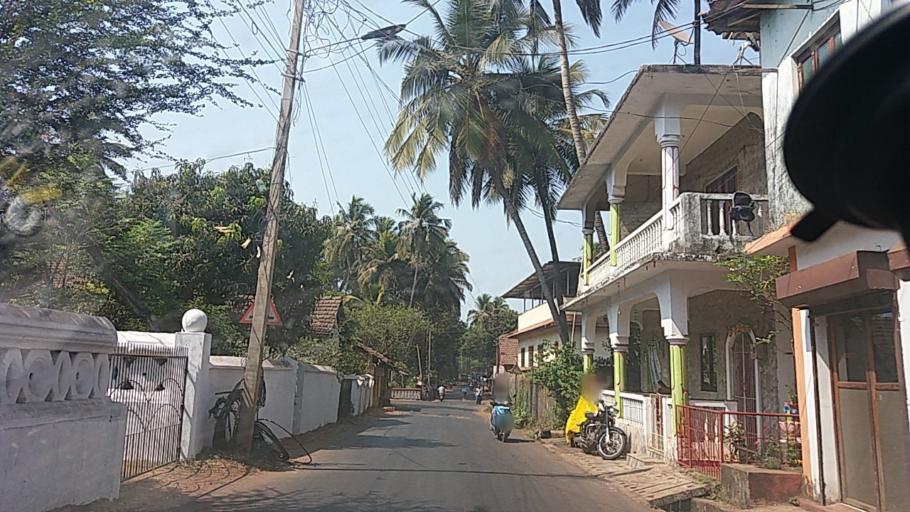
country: IN
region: Goa
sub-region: North Goa
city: Saligao
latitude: 15.5403
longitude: 73.7897
